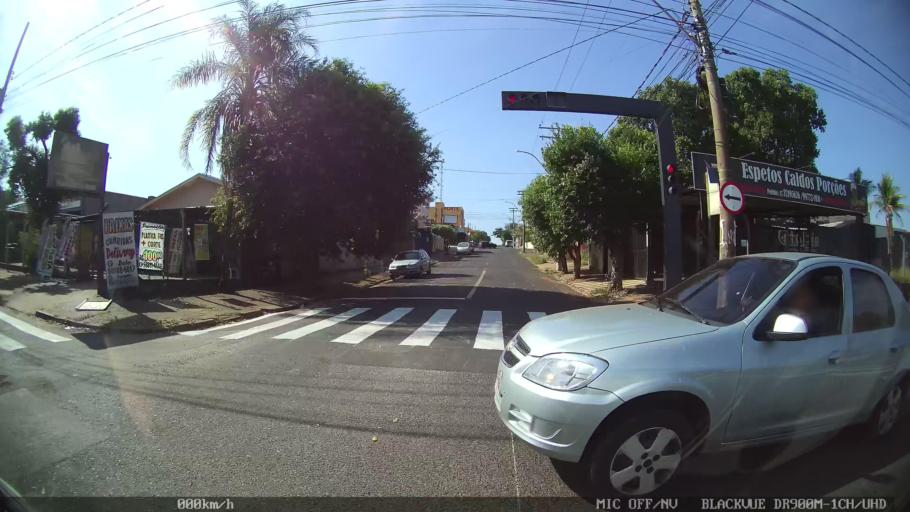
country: BR
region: Sao Paulo
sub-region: Sao Jose Do Rio Preto
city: Sao Jose do Rio Preto
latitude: -20.7953
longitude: -49.4021
